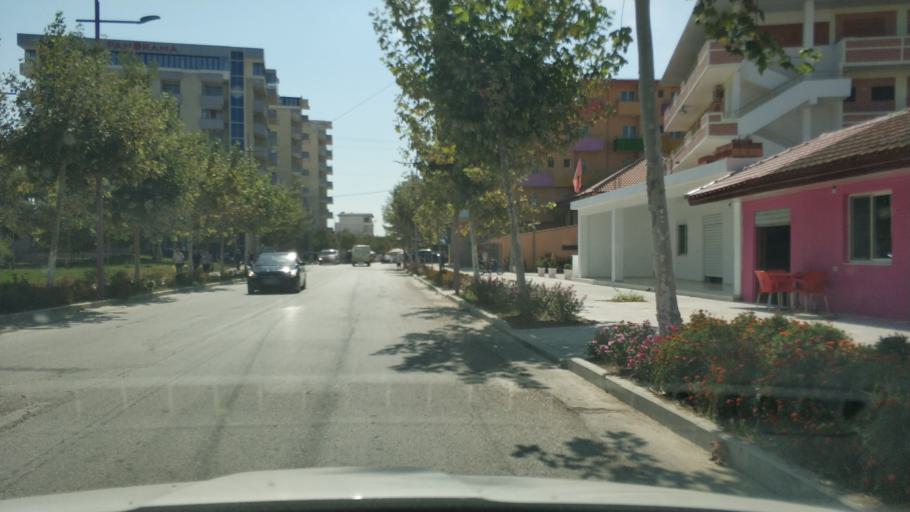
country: AL
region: Fier
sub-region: Rrethi i Lushnjes
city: Divjake
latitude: 40.9971
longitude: 19.5324
